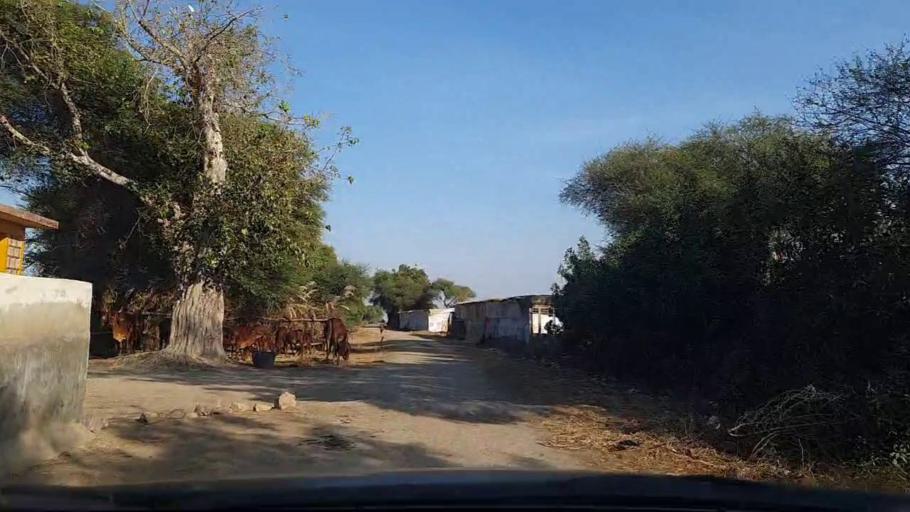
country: PK
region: Sindh
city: Mirpur Sakro
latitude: 24.5242
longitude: 67.6389
